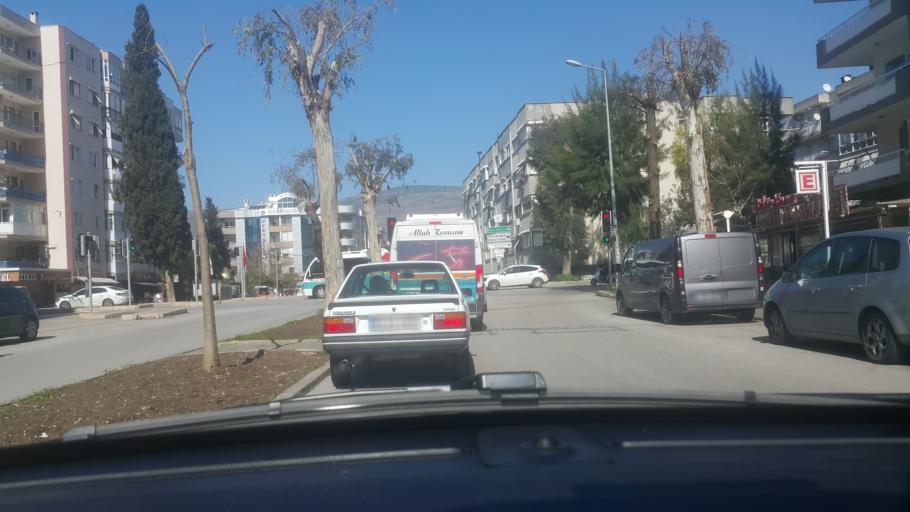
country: TR
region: Izmir
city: Bornova
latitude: 38.4620
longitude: 27.1992
